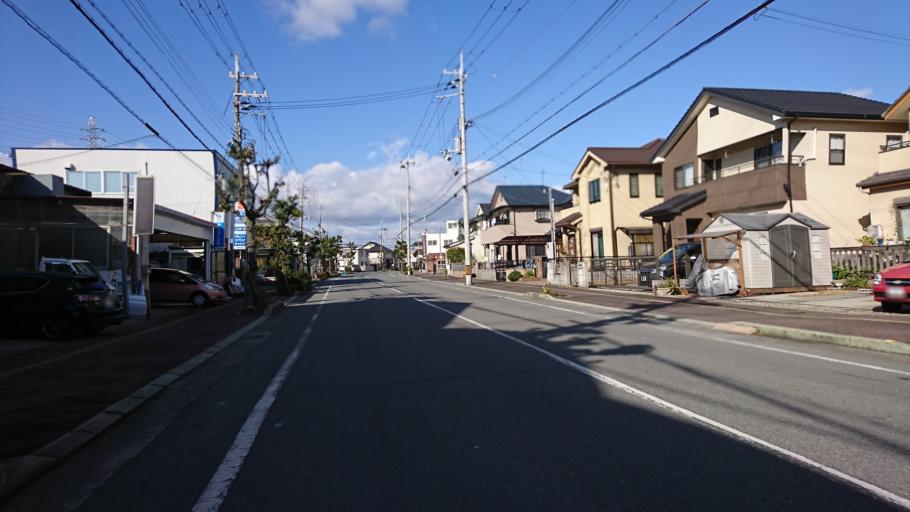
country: JP
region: Hyogo
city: Kakogawacho-honmachi
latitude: 34.7546
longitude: 134.7988
